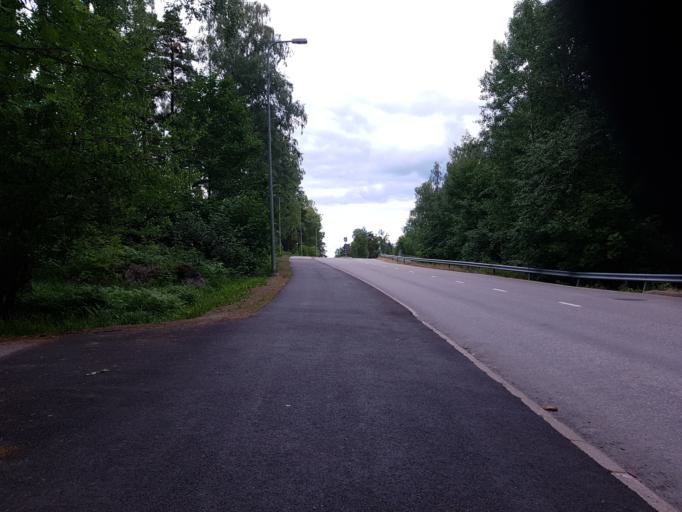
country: FI
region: Uusimaa
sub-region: Helsinki
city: Teekkarikylae
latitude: 60.2793
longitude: 24.8750
